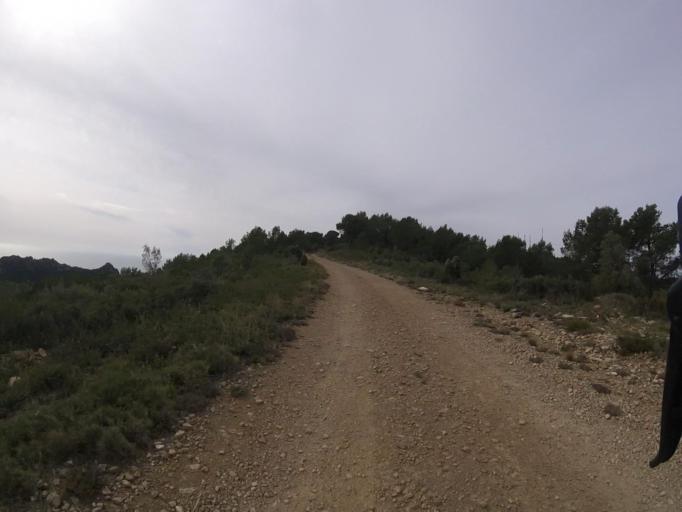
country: ES
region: Valencia
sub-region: Provincia de Castello
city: Benicassim
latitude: 40.0914
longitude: 0.0378
